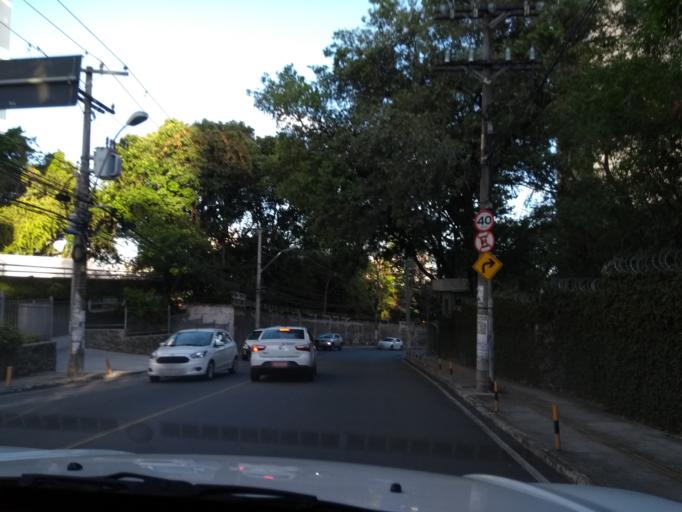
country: BR
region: Bahia
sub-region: Salvador
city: Salvador
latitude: -12.9962
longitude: -38.4873
